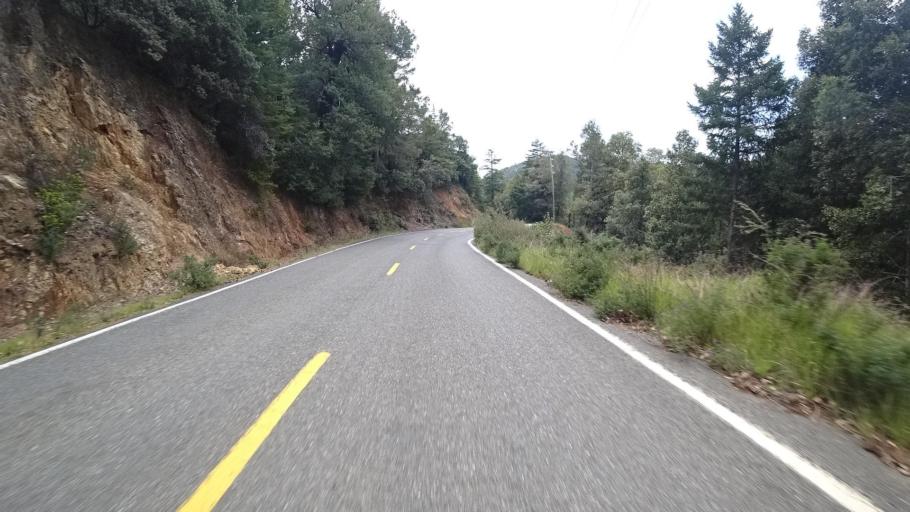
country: US
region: California
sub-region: Humboldt County
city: Redway
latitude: 40.0410
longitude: -124.0227
